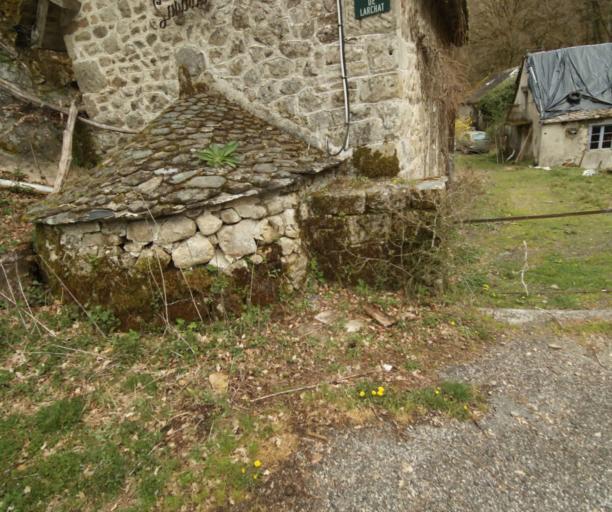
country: FR
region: Limousin
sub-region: Departement de la Correze
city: Argentat
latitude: 45.1936
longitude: 1.9766
